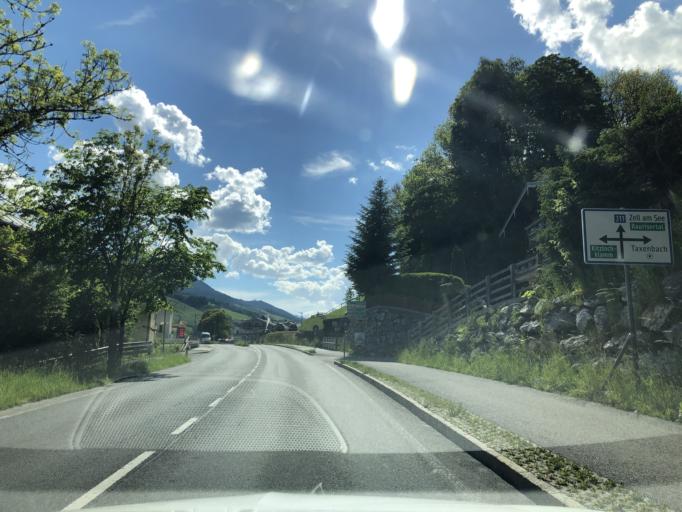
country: AT
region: Salzburg
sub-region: Politischer Bezirk Zell am See
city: Taxenbach
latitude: 47.2941
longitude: 12.9708
